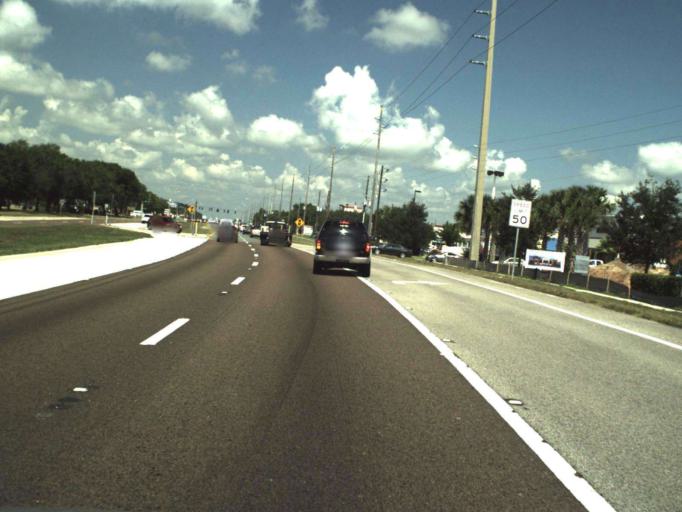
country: US
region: Florida
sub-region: Lake County
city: Mount Dora
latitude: 28.8241
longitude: -81.6394
